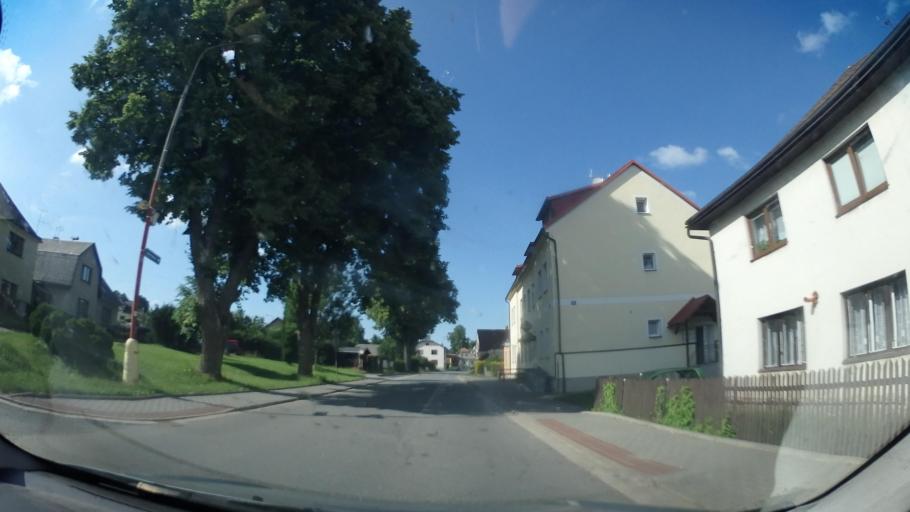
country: CZ
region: Vysocina
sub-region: Okres Zd'ar nad Sazavou
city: Svratka
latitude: 49.7200
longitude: 16.0353
